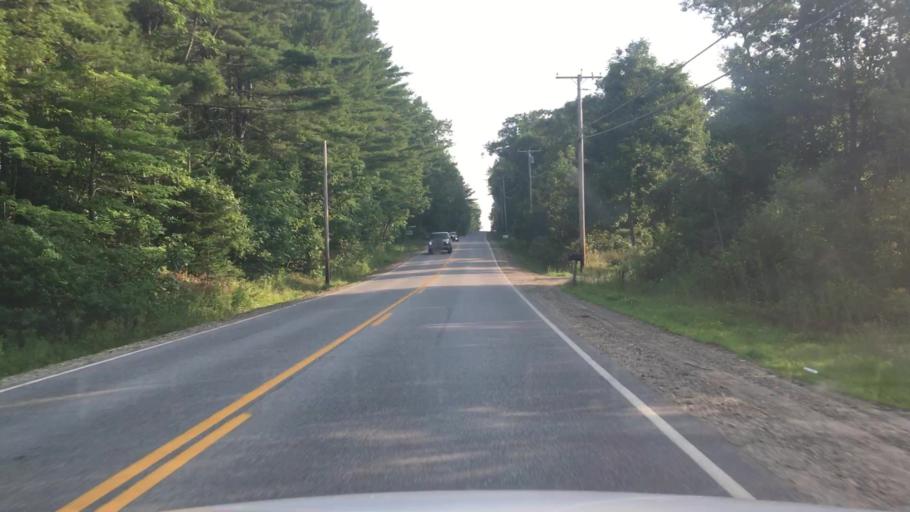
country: US
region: Maine
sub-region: Androscoggin County
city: Lisbon Falls
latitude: 43.9559
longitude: -70.0610
